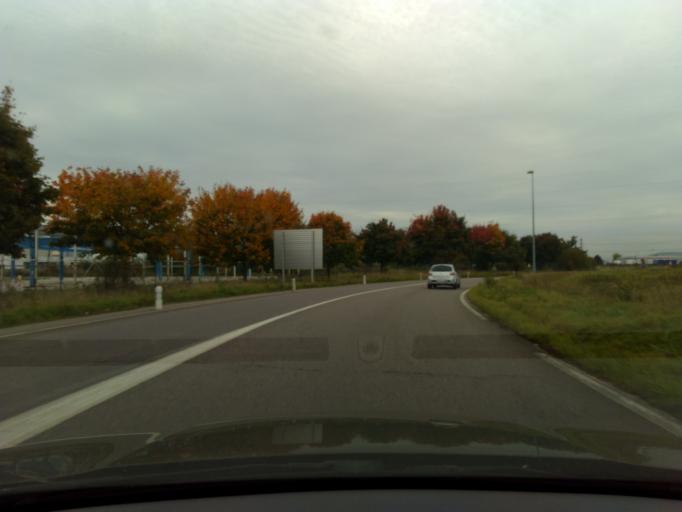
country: FR
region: Lorraine
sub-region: Departement de la Moselle
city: Maizieres-les-Metz
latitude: 49.2032
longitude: 6.1495
